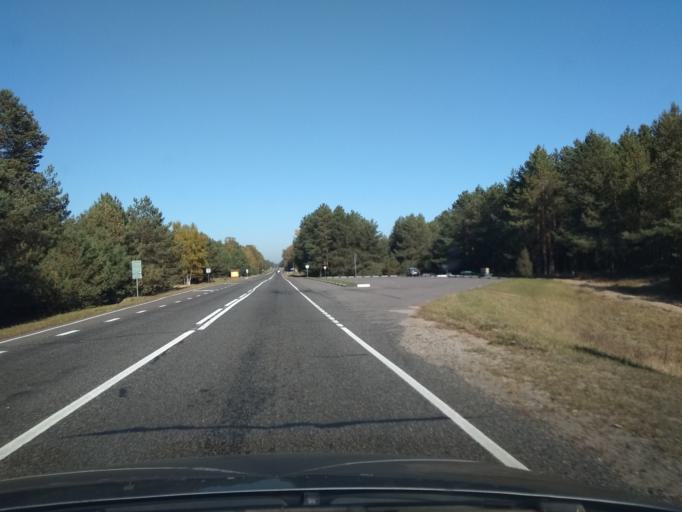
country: BY
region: Brest
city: Kobryn
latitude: 52.0731
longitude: 24.2829
